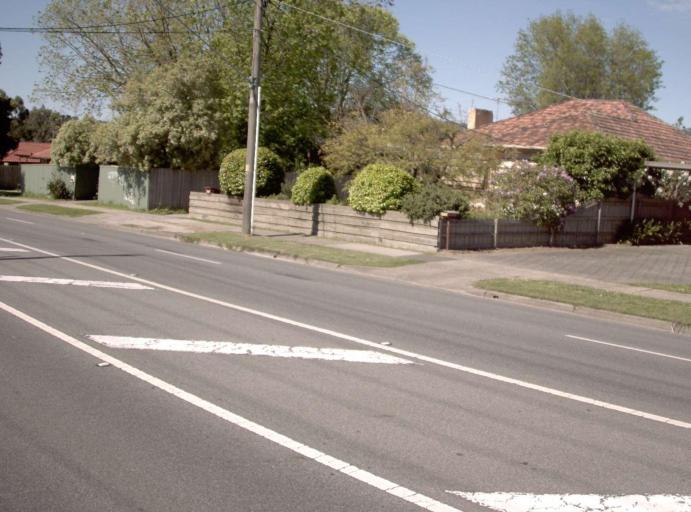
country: AU
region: Victoria
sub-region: Knox
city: Bayswater
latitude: -37.8706
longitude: 145.2605
